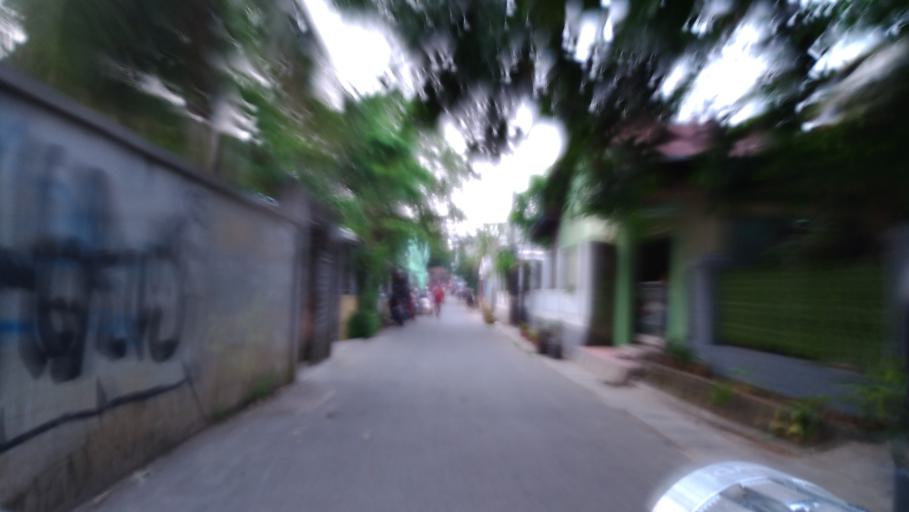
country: ID
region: West Java
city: Depok
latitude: -6.3571
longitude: 106.8706
